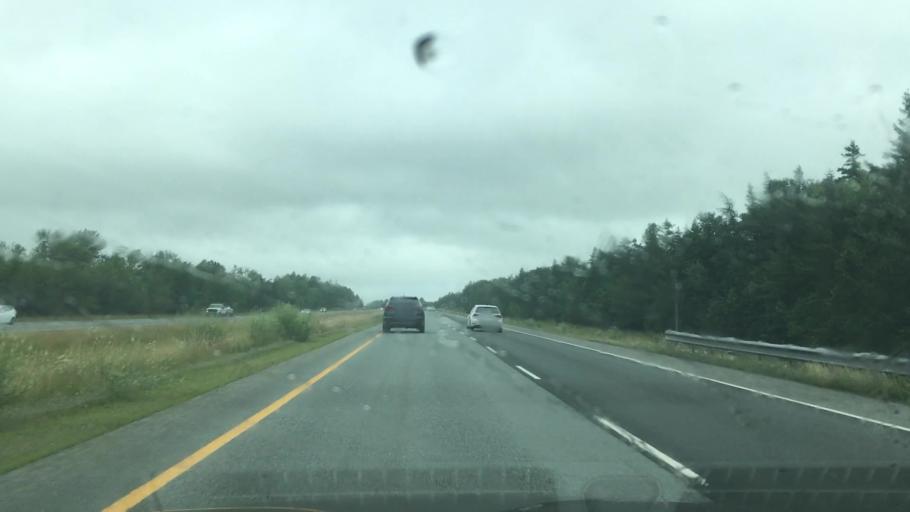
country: CA
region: Nova Scotia
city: Truro
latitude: 45.2609
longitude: -63.2922
